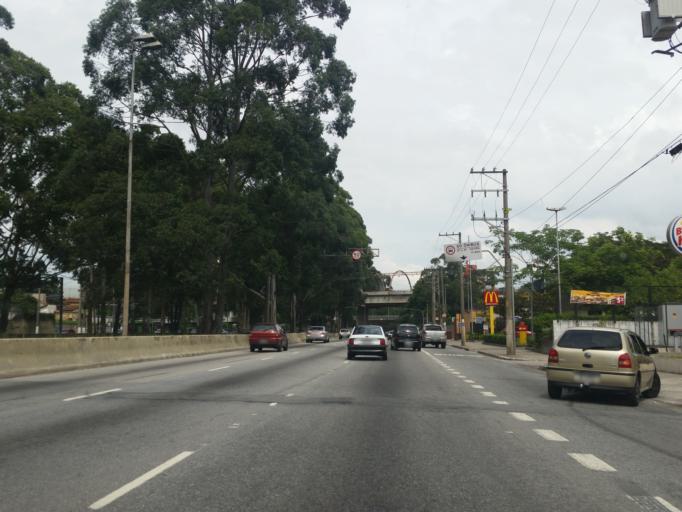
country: BR
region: Sao Paulo
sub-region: Ferraz De Vasconcelos
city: Ferraz de Vasconcelos
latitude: -23.5398
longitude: -46.4501
